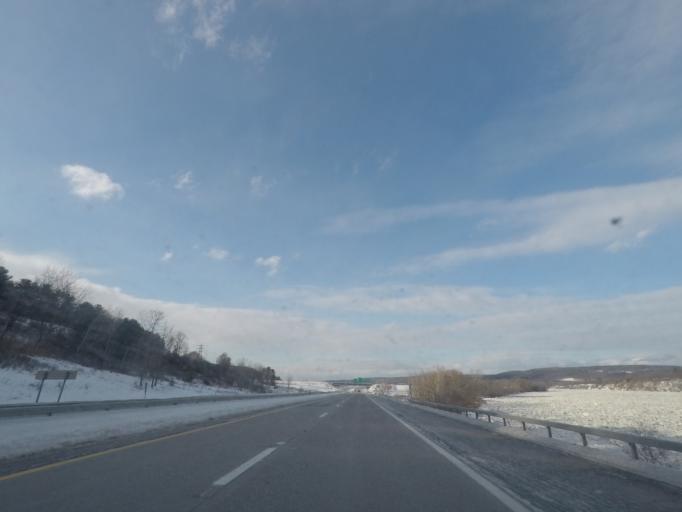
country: US
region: New York
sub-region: Schenectady County
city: Scotia
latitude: 42.8368
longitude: -73.9993
